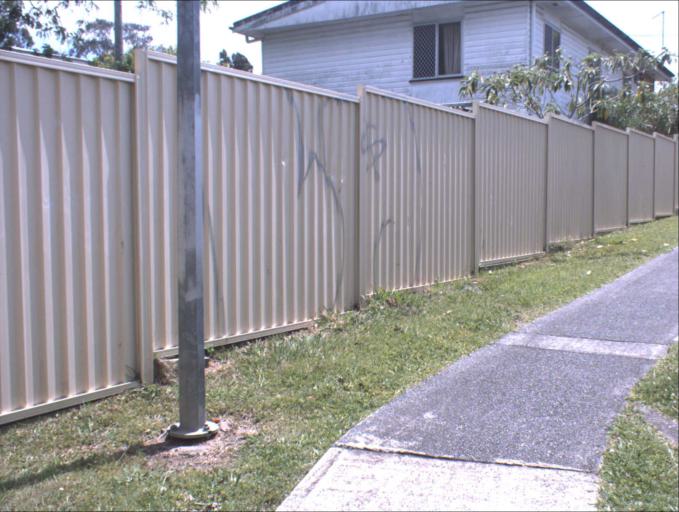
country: AU
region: Queensland
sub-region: Logan
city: Woodridge
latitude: -27.6363
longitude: 153.0986
